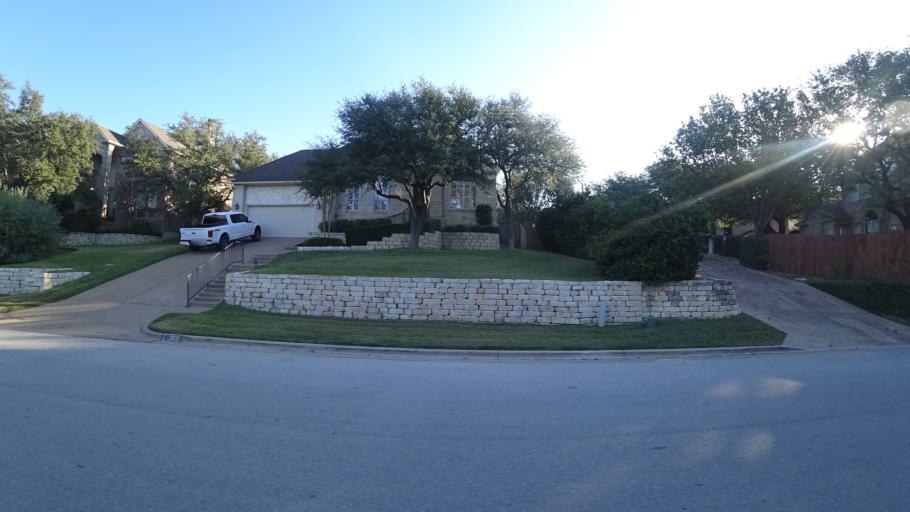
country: US
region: Texas
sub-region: Travis County
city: Hudson Bend
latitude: 30.3753
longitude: -97.8831
